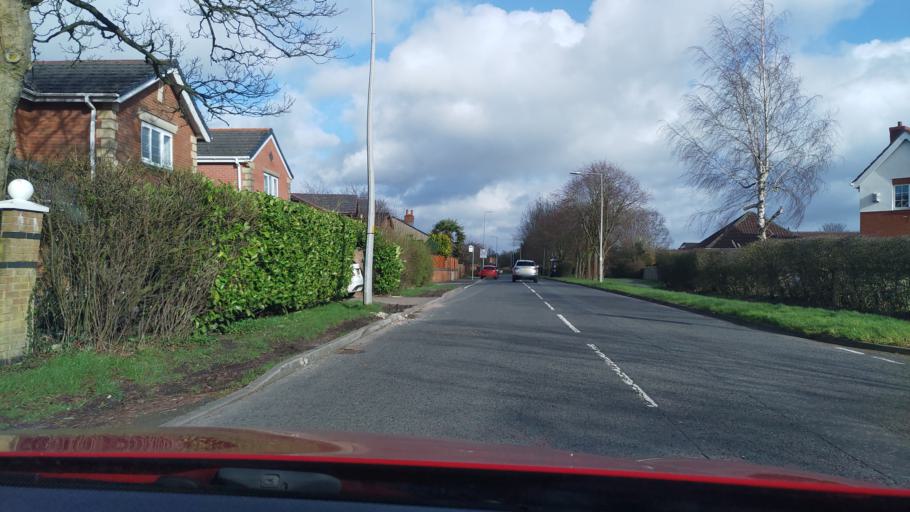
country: GB
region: England
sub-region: Lancashire
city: Goosnargh
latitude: 53.7863
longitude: -2.6788
